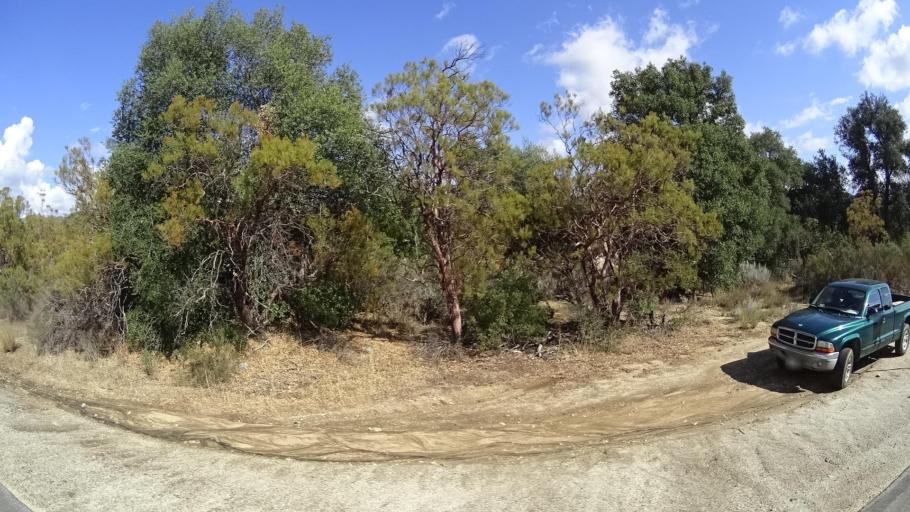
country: US
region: California
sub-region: San Diego County
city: Pine Valley
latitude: 32.7293
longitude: -116.4955
